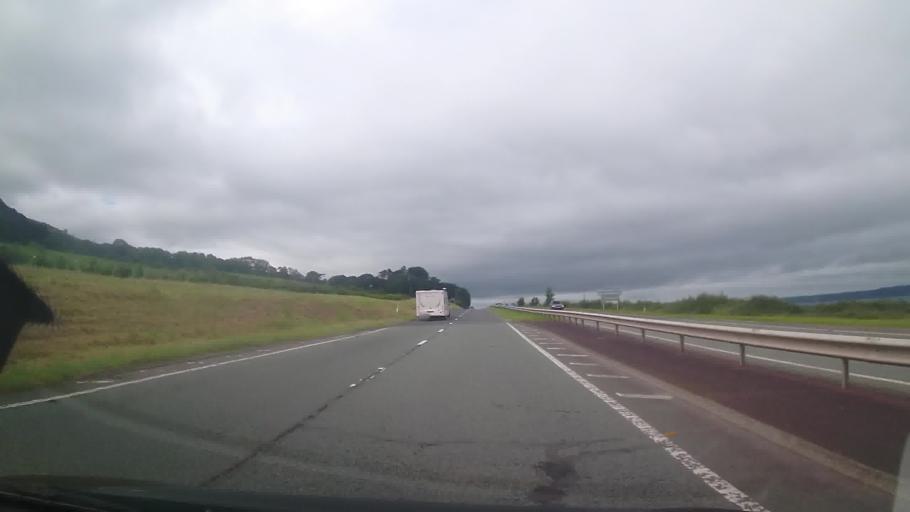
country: GB
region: Wales
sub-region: Gwynedd
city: Aber
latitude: 53.2328
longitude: -4.0246
